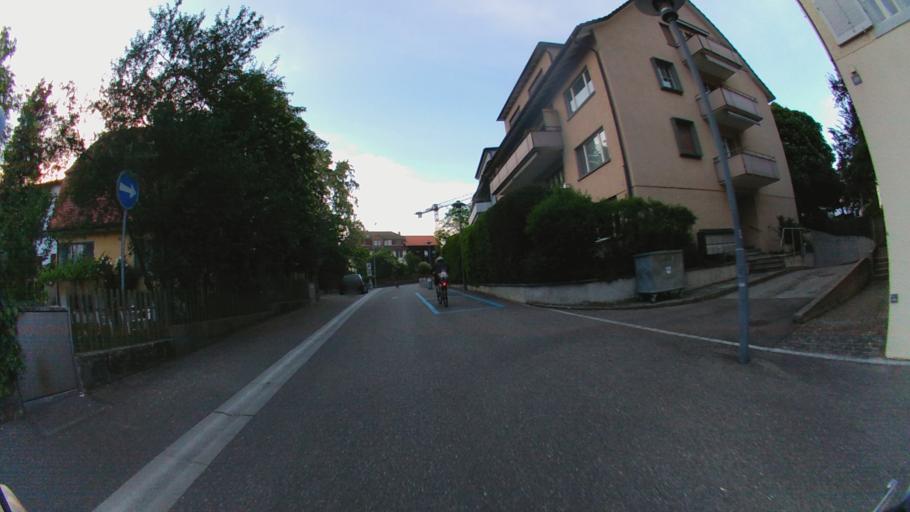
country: CH
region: Zurich
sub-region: Bezirk Meilen
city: Kuesnacht
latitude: 47.3182
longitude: 8.5837
